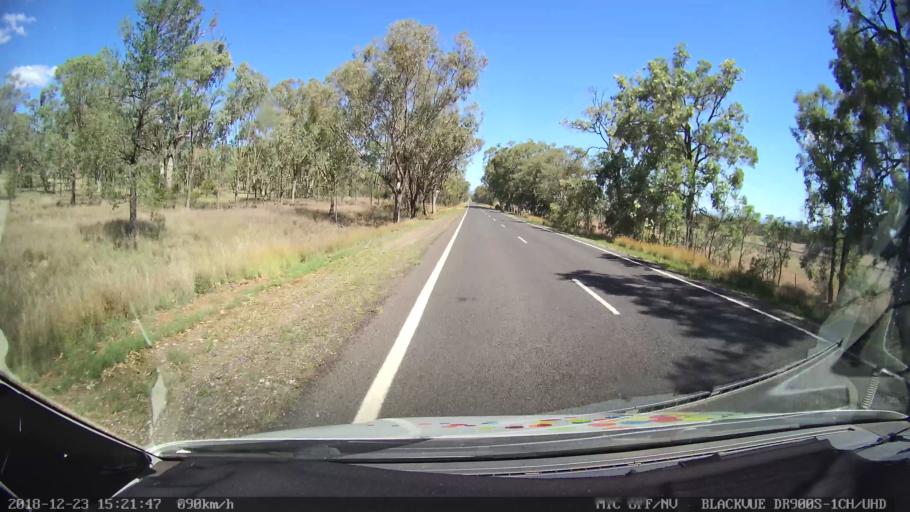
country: AU
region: New South Wales
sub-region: Tamworth Municipality
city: Manilla
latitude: -30.8607
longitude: 150.7991
